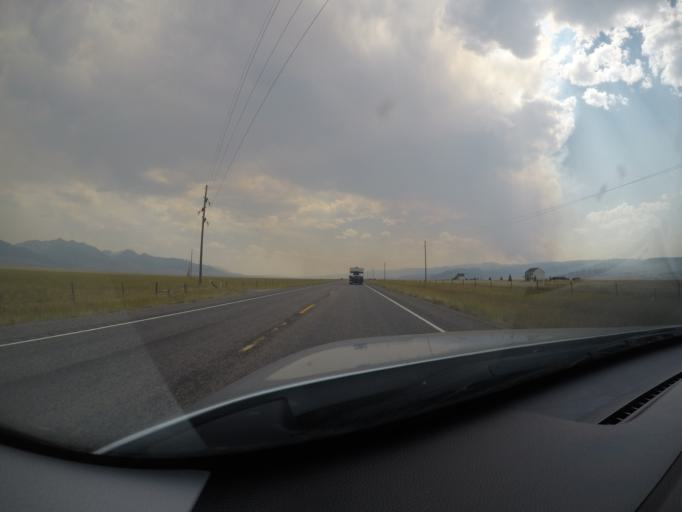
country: US
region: Montana
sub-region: Madison County
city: Virginia City
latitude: 45.1628
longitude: -111.6786
